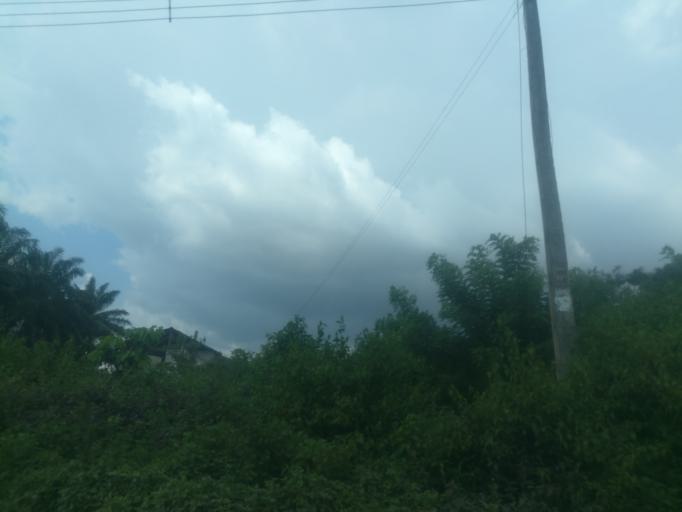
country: NG
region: Oyo
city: Ido
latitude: 7.4113
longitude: 3.8218
